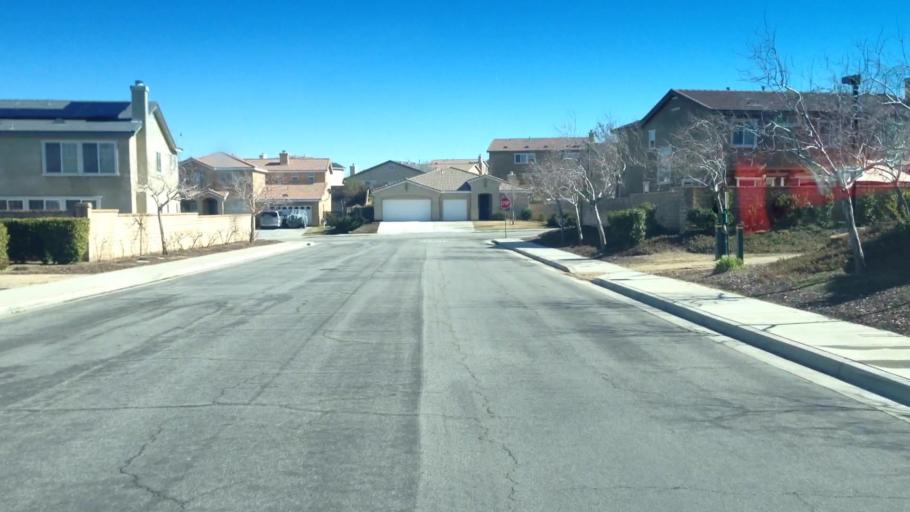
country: US
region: California
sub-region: Los Angeles County
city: Desert View Highlands
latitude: 34.5617
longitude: -118.1733
